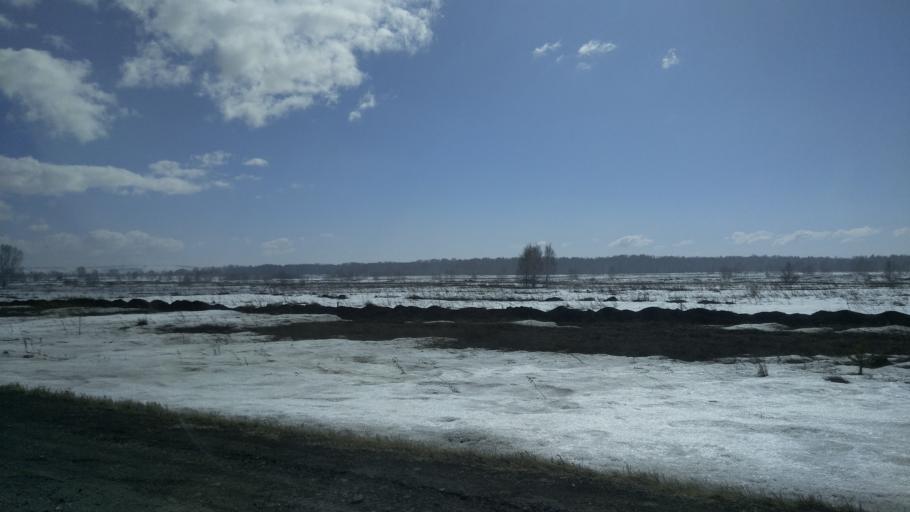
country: RU
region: Kemerovo
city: Yurga
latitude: 55.6835
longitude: 85.0106
